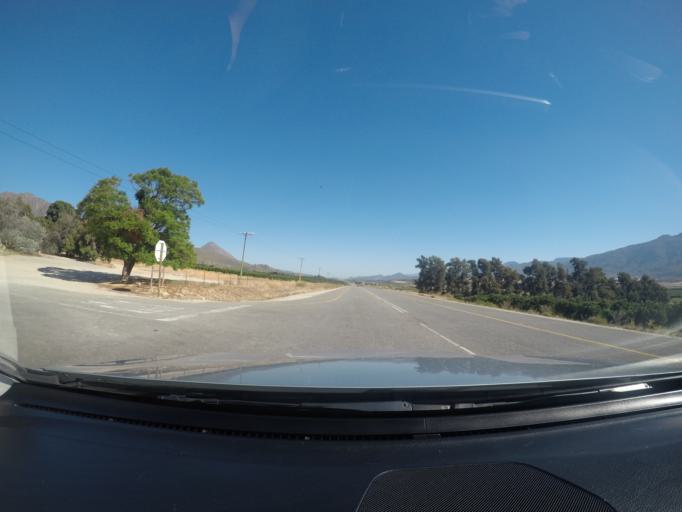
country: ZA
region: Western Cape
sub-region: West Coast District Municipality
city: Clanwilliam
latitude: -32.5720
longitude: 18.9868
